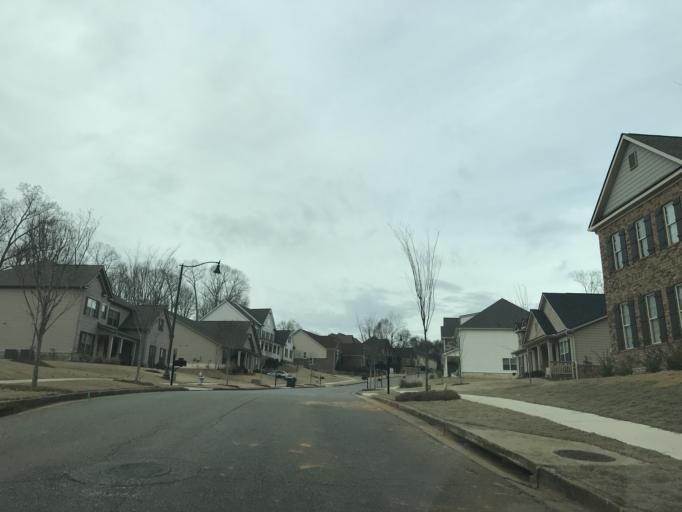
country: US
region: Georgia
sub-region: Cherokee County
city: Canton
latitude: 34.2041
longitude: -84.3941
